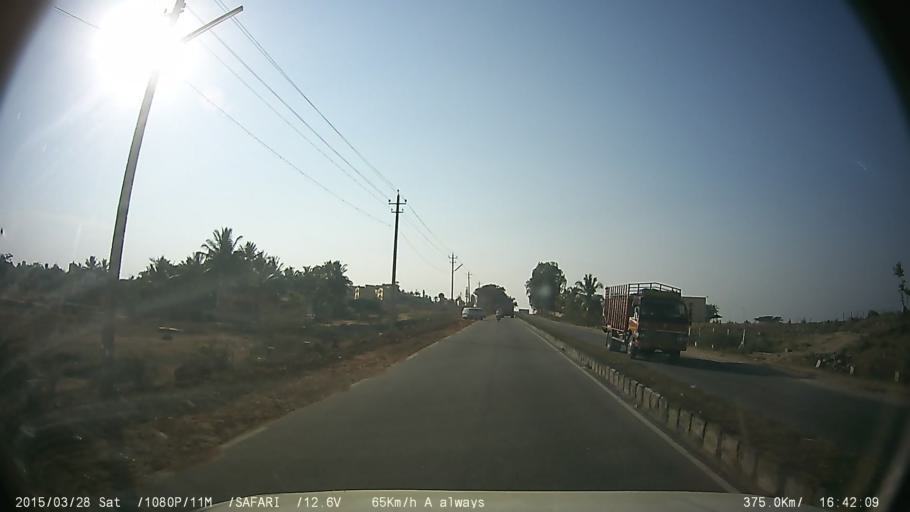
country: IN
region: Karnataka
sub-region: Mandya
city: Shrirangapattana
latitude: 12.3997
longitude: 76.5781
